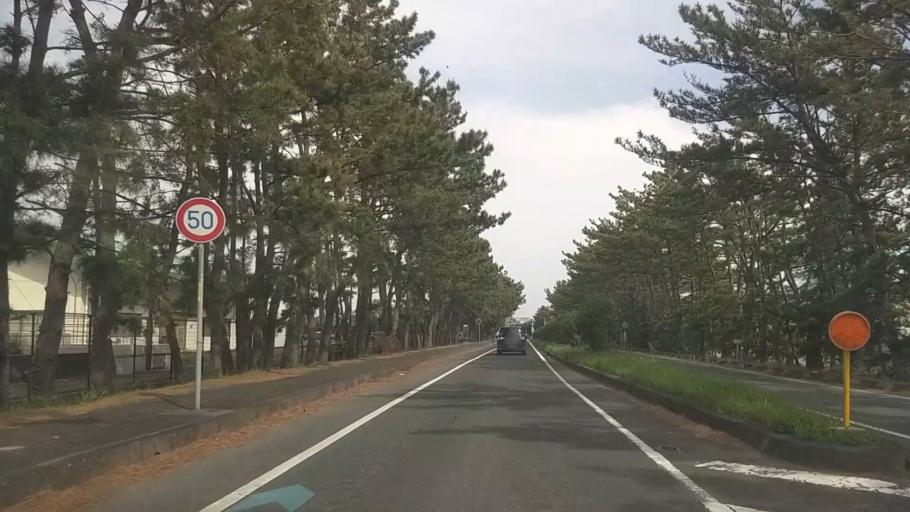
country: JP
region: Shizuoka
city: Kosai-shi
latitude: 34.6973
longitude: 137.6047
